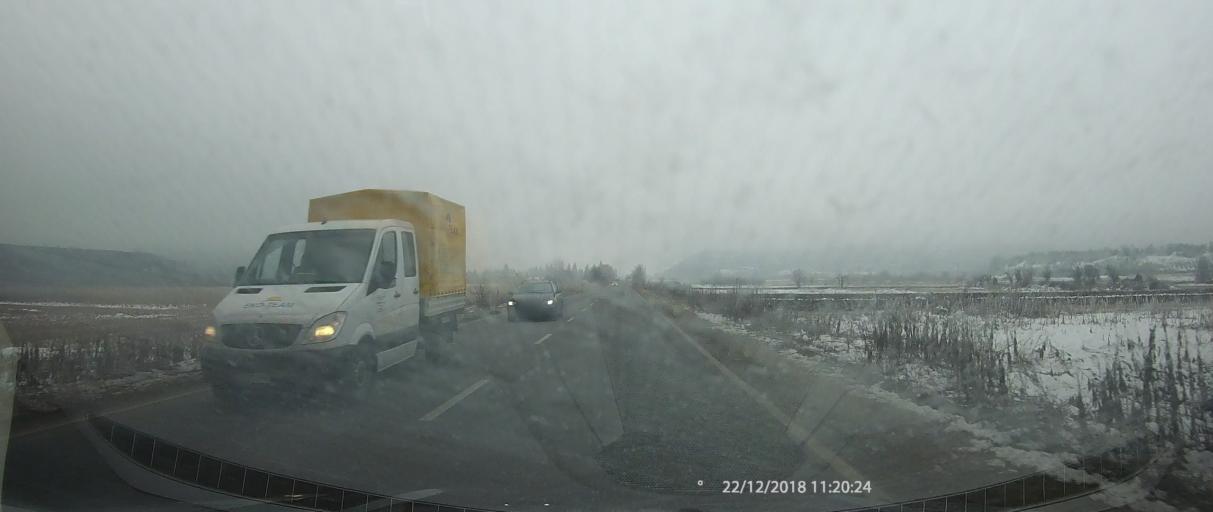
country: BG
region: Kyustendil
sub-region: Obshtina Kyustendil
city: Kyustendil
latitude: 42.2648
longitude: 22.8157
